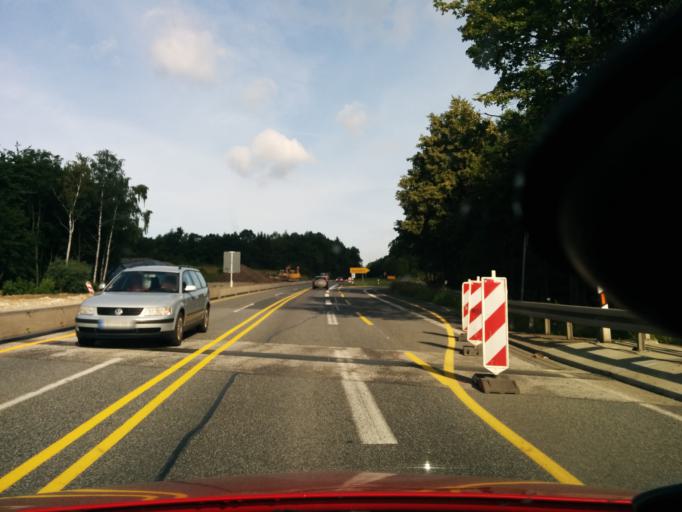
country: DE
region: Lower Saxony
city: Goslar
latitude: 51.9182
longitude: 10.4460
